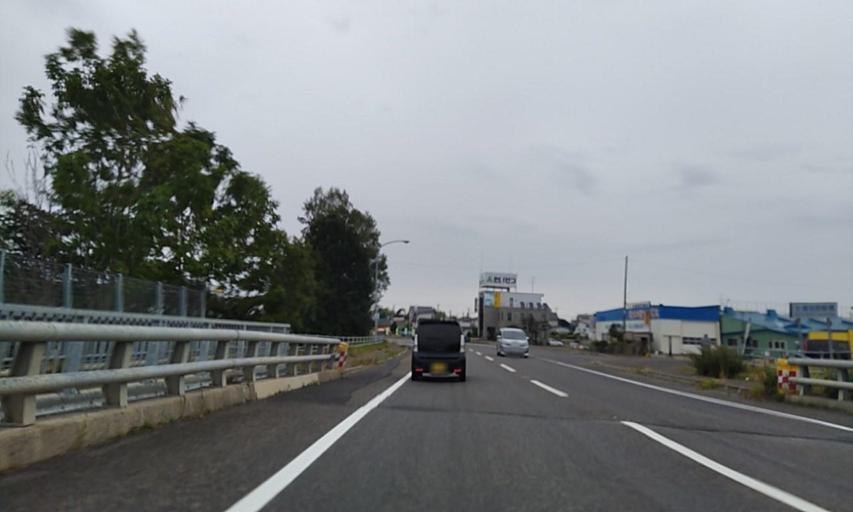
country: JP
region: Hokkaido
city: Bihoro
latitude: 43.9138
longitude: 144.1661
